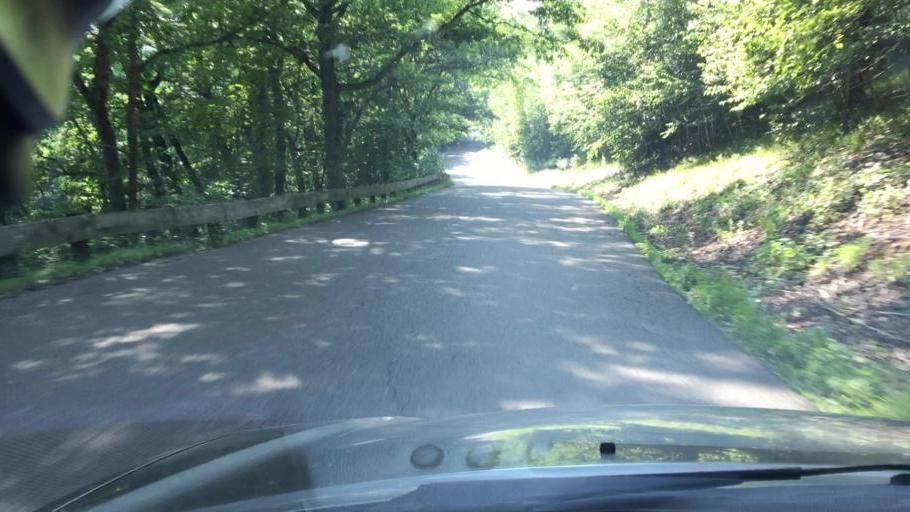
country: US
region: Pennsylvania
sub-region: Carbon County
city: Jim Thorpe
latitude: 40.8745
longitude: -75.7418
